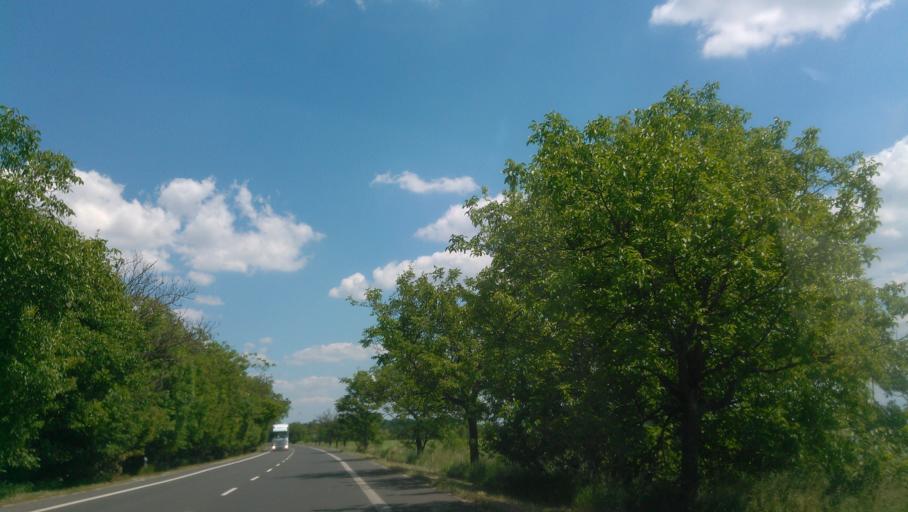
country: SK
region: Trnavsky
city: Samorin
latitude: 48.0033
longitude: 17.3834
